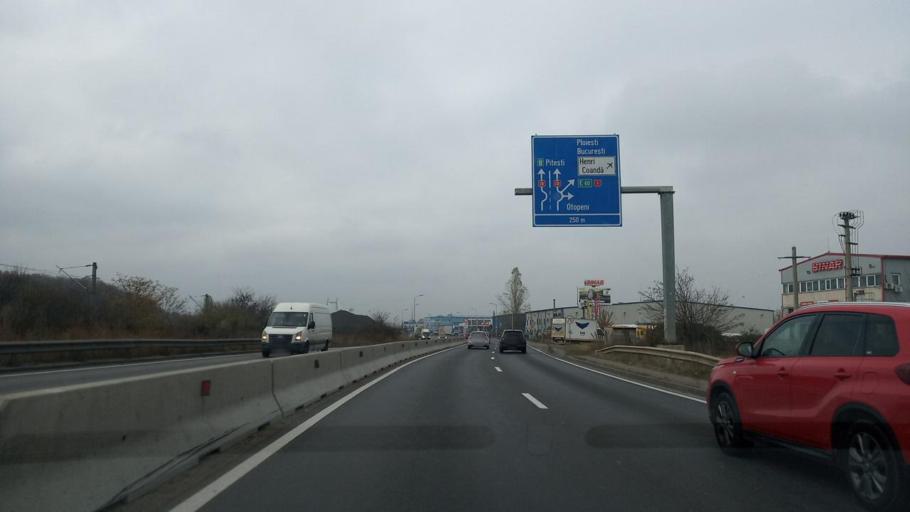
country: RO
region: Ilfov
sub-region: Comuna Otopeni
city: Otopeni
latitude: 44.5385
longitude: 26.0877
